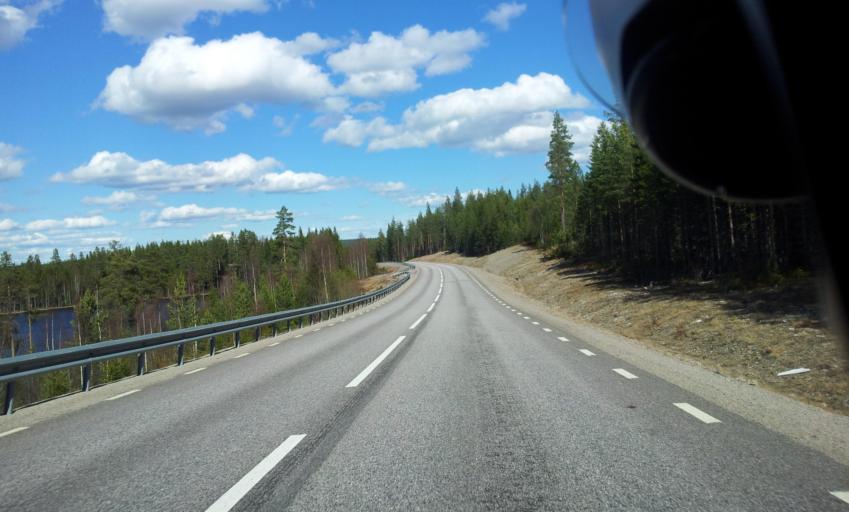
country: SE
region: Gaevleborg
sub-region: Bollnas Kommun
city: Vittsjo
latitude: 61.1329
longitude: 15.8773
